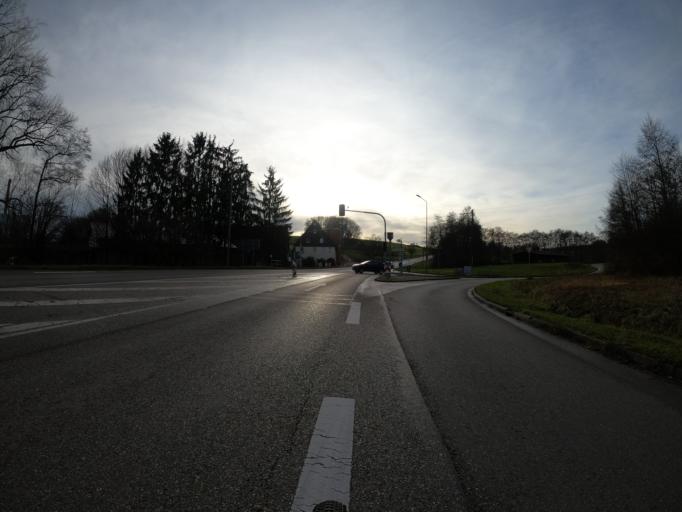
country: DE
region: Baden-Wuerttemberg
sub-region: Regierungsbezirk Stuttgart
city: Goeppingen
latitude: 48.6857
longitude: 9.6686
